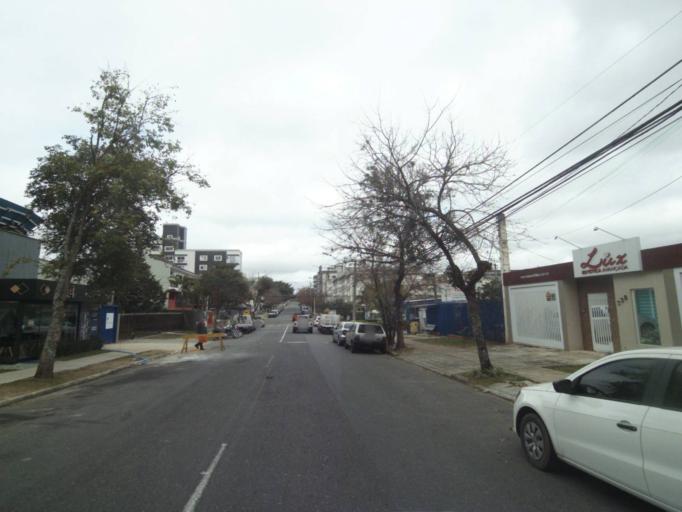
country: BR
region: Parana
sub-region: Curitiba
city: Curitiba
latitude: -25.4568
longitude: -49.2958
